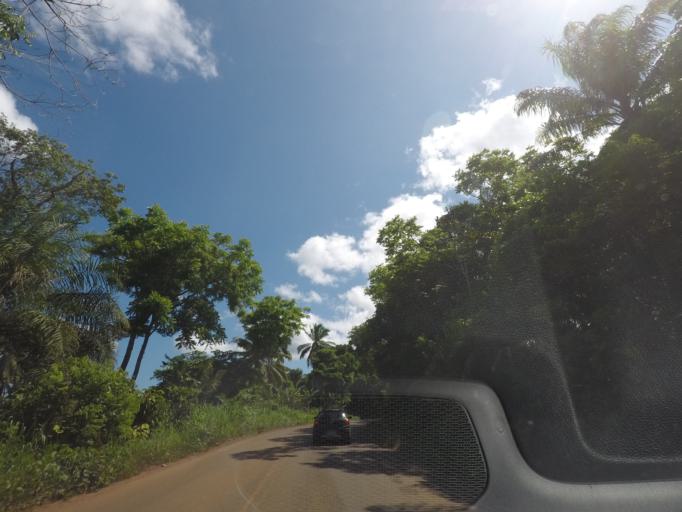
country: BR
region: Bahia
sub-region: Taperoa
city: Taperoa
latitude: -13.5888
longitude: -39.1069
